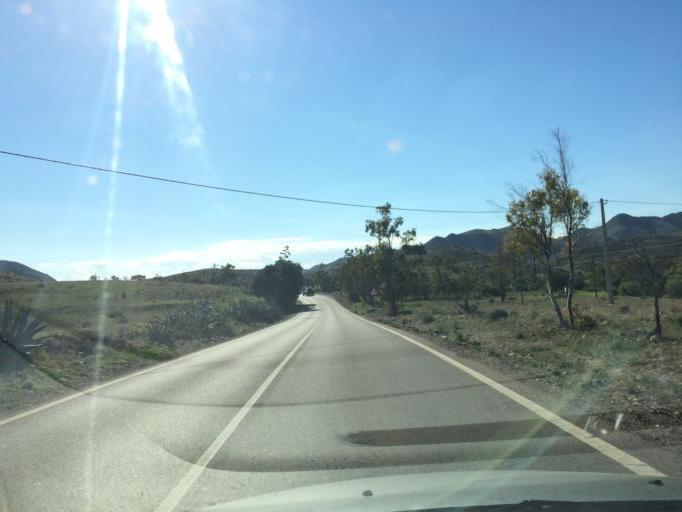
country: ES
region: Andalusia
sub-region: Provincia de Almeria
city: San Jose
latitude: 36.7872
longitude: -2.1091
